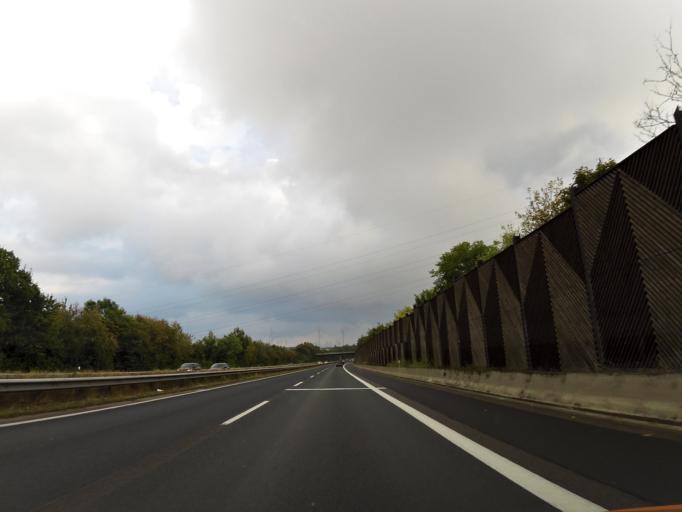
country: DE
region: Rheinland-Pfalz
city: Dorth
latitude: 50.1527
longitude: 7.5954
